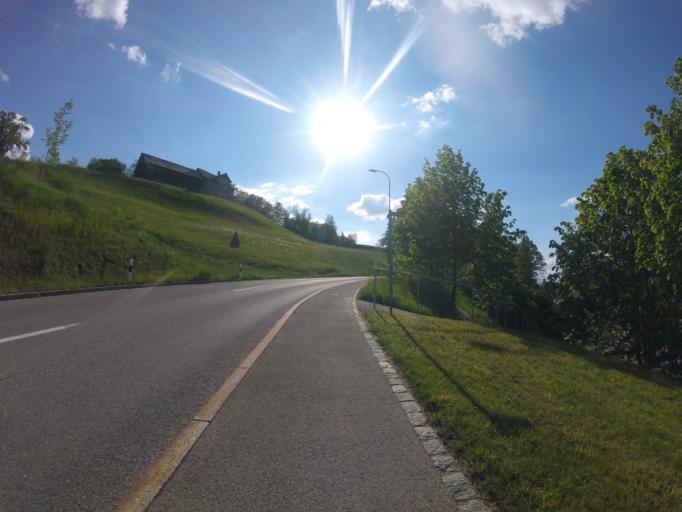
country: CH
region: Saint Gallen
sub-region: Wahlkreis Toggenburg
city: Mogelsberg
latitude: 47.3634
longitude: 9.1422
